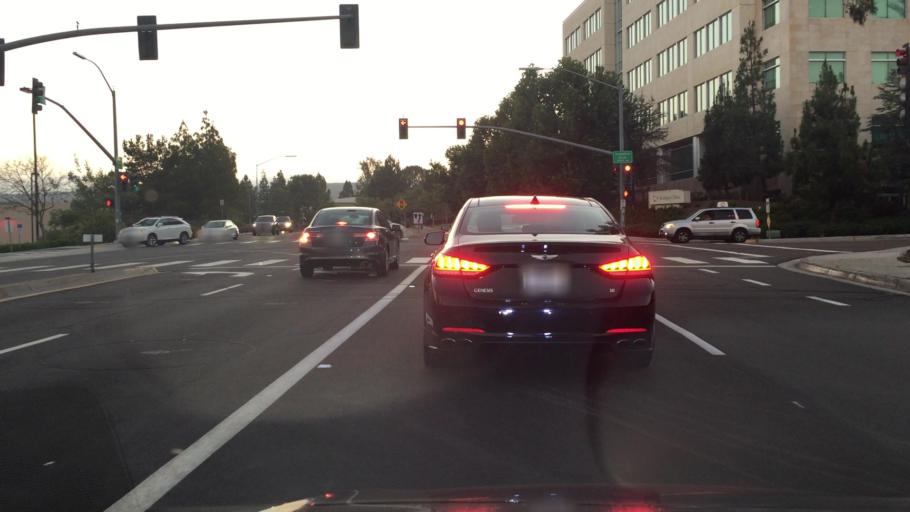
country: US
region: California
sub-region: San Diego County
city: Poway
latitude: 32.9887
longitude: -117.0766
